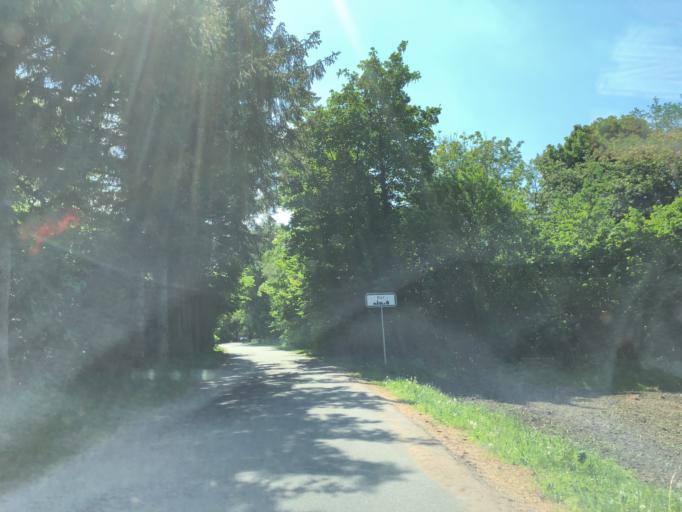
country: DK
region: Central Jutland
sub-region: Holstebro Kommune
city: Ulfborg
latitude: 56.3699
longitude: 8.4328
